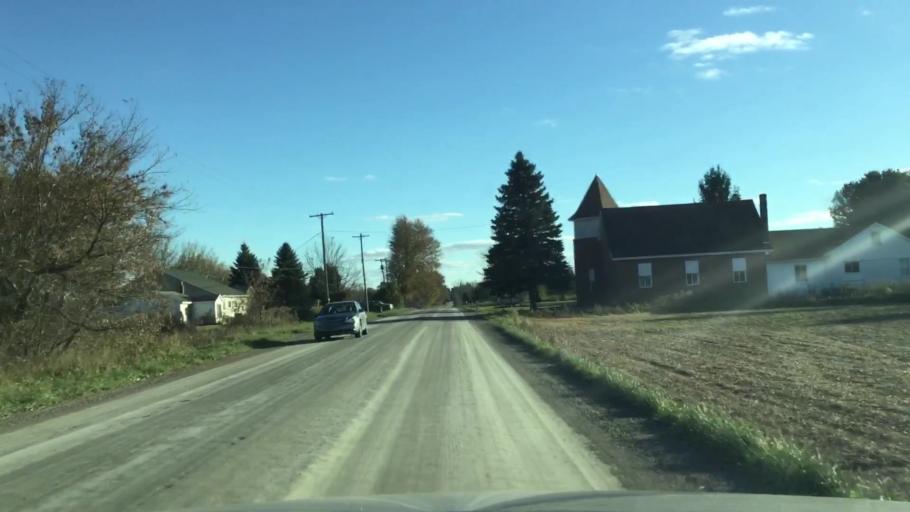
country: US
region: Michigan
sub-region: Lapeer County
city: Lapeer
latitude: 43.0687
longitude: -83.2272
